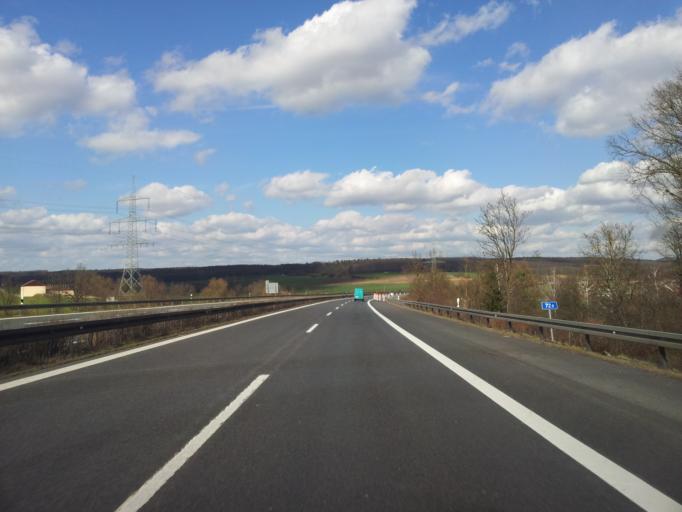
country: DE
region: Bavaria
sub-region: Upper Franconia
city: Memmelsdorf
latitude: 49.9599
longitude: 10.9859
